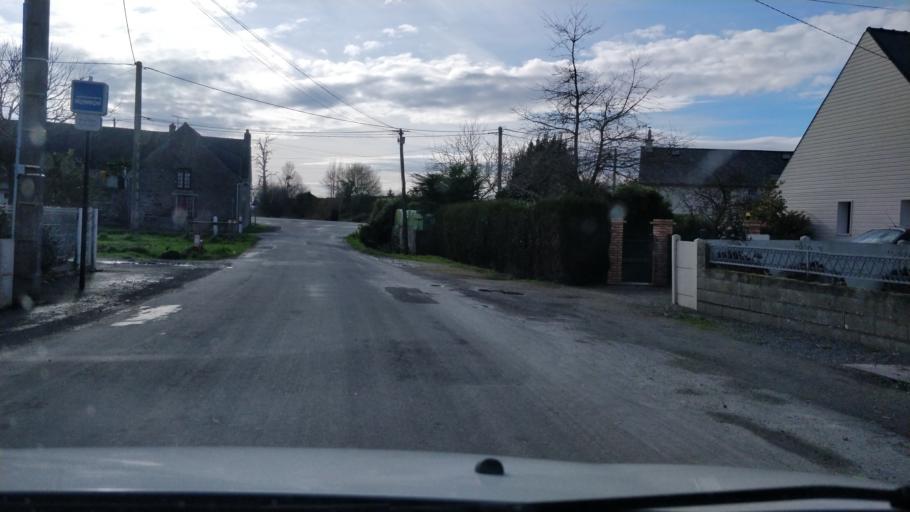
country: FR
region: Brittany
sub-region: Departement d'Ille-et-Vilaine
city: Hirel
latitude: 48.5797
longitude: -1.8158
